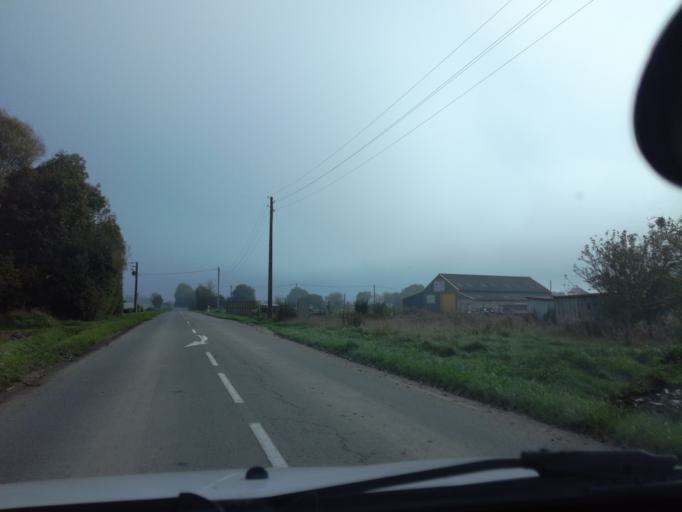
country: FR
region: Brittany
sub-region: Departement d'Ille-et-Vilaine
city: Cherrueix
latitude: 48.6002
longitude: -1.6999
